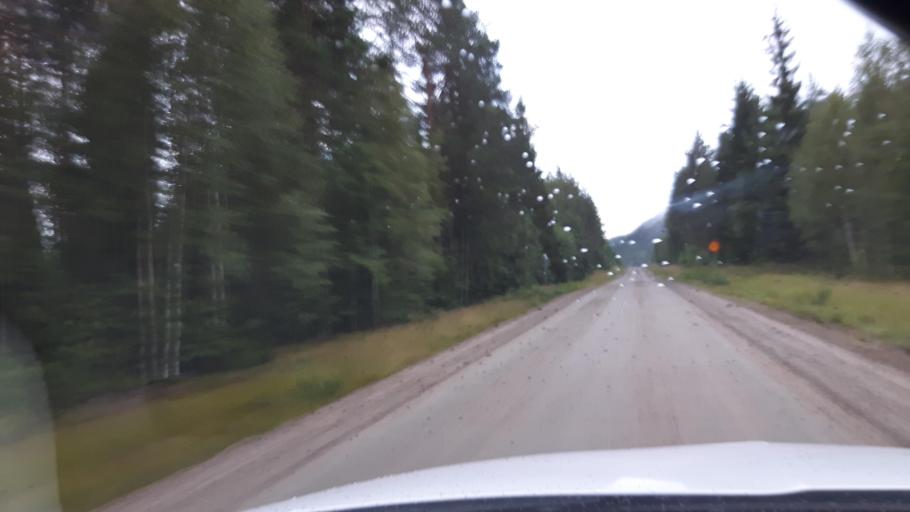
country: SE
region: Gaevleborg
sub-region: Ljusdals Kommun
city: Farila
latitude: 62.0408
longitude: 15.8217
